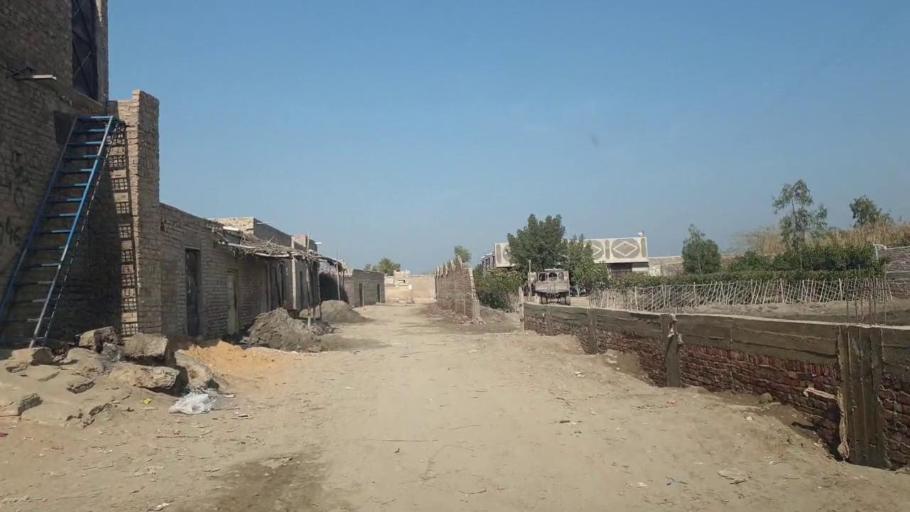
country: PK
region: Sindh
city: Sakrand
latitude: 26.0717
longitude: 68.4164
